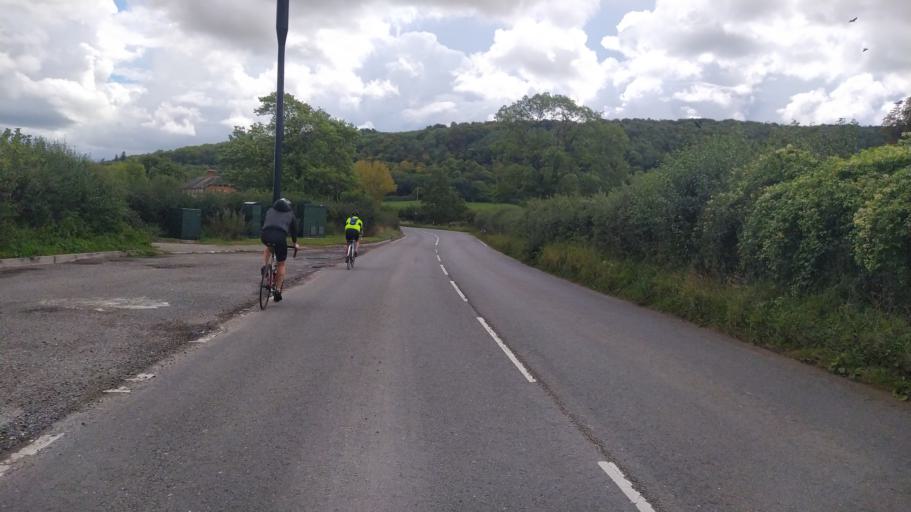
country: GB
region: England
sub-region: Dorset
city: Manston
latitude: 50.8935
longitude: -2.2391
